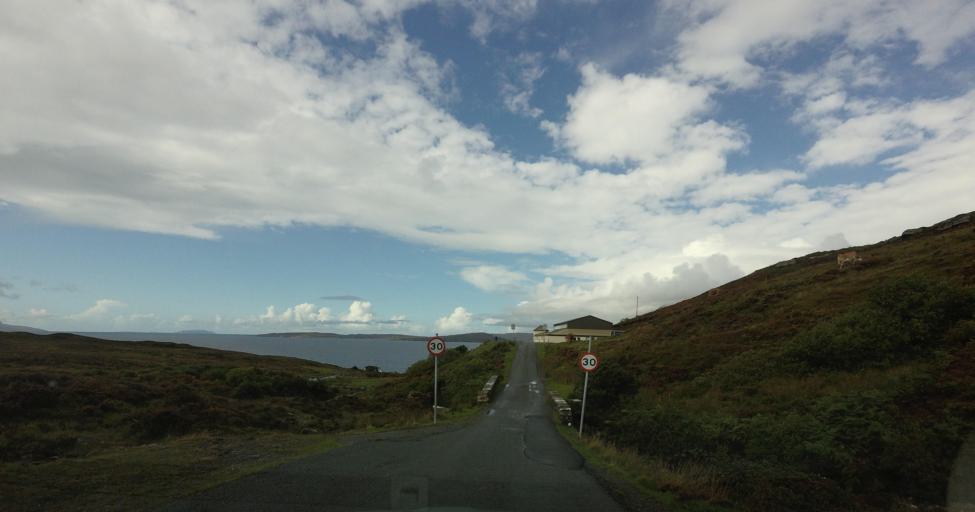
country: GB
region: Scotland
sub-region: Highland
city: Isle of Skye
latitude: 57.1451
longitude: -6.1006
